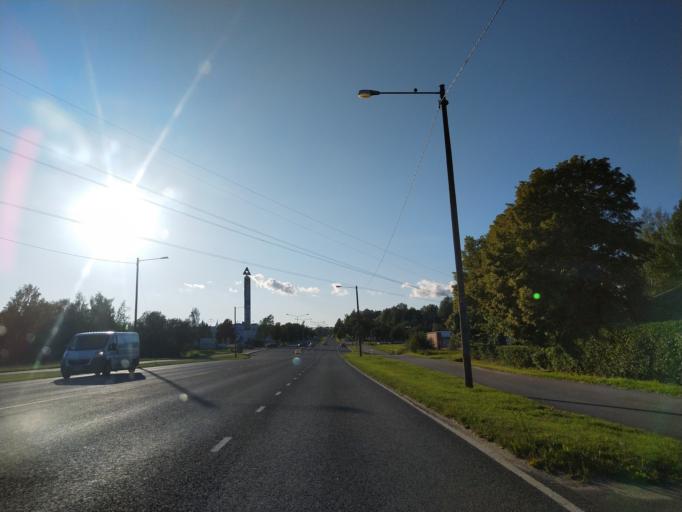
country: FI
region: Varsinais-Suomi
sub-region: Turku
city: Kaarina
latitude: 60.4447
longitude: 22.3304
